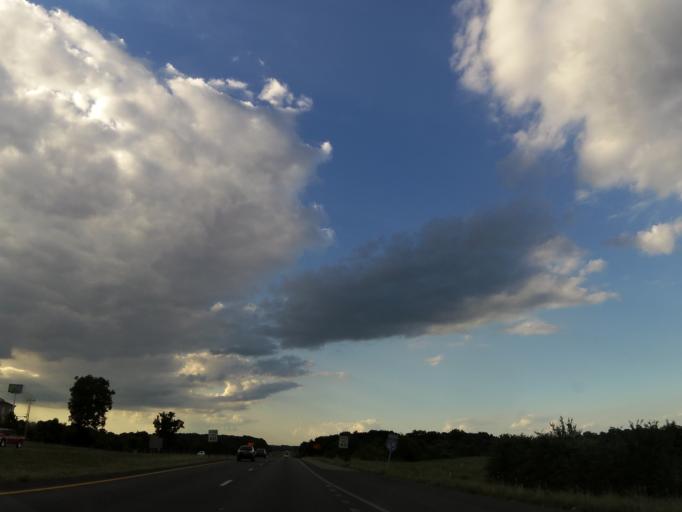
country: US
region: Tennessee
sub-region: Maury County
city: Spring Hill
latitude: 35.6446
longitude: -86.8934
